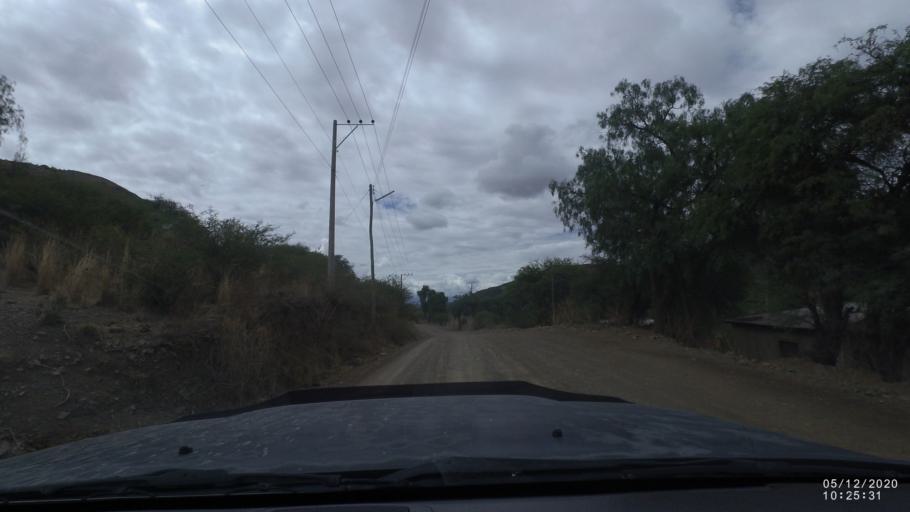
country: BO
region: Cochabamba
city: Sipe Sipe
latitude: -17.5184
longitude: -66.2875
